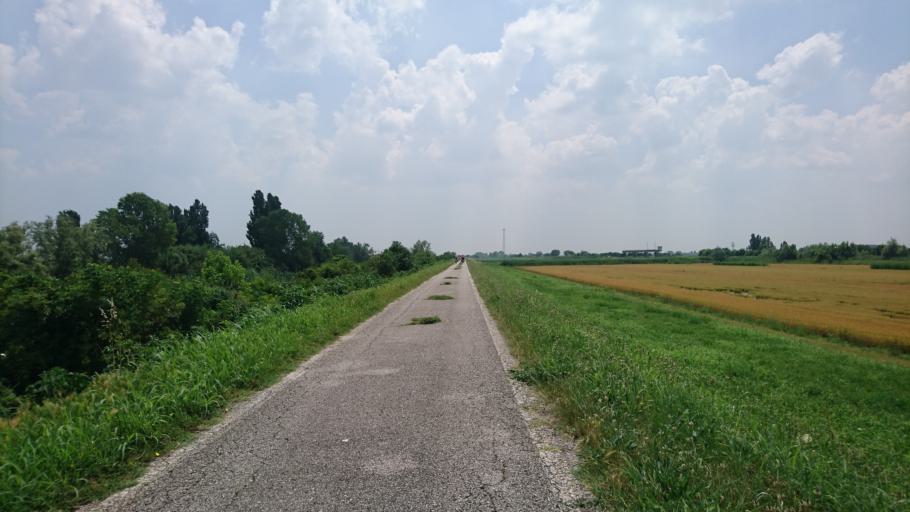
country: IT
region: Veneto
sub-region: Provincia di Venezia
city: Valli
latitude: 45.2125
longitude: 12.1702
